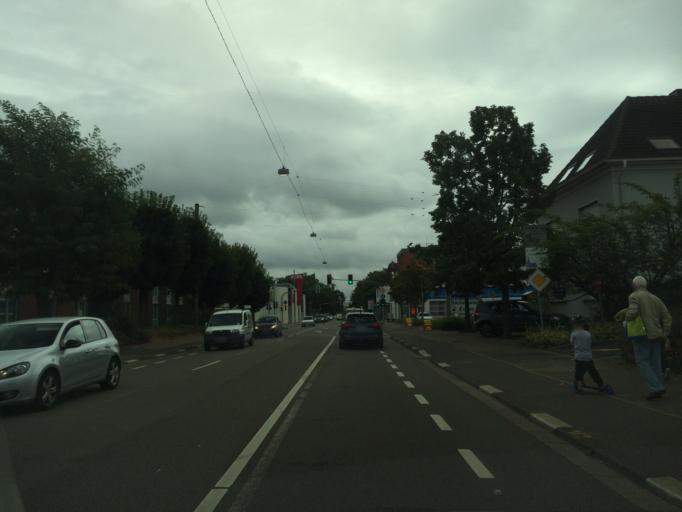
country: DE
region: Saarland
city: Dillingen
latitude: 49.3568
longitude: 6.7202
